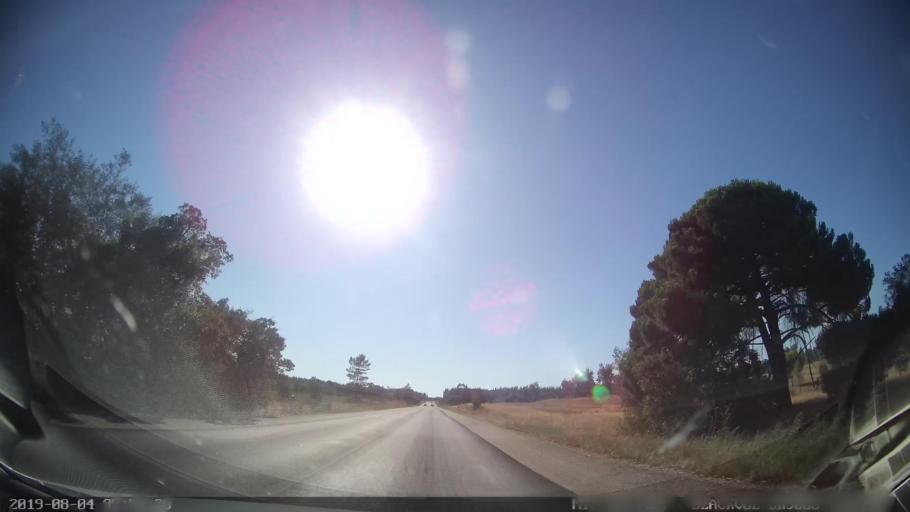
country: PT
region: Portalegre
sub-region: Gaviao
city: Gaviao
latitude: 39.4471
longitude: -7.8905
